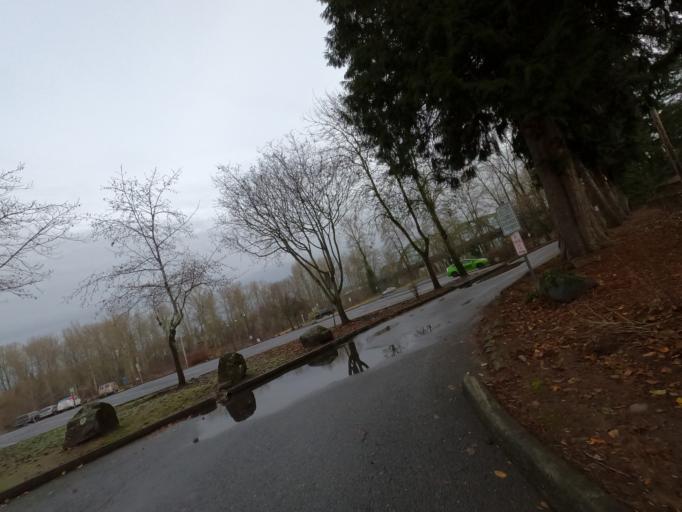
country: US
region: Oregon
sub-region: Clackamas County
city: West Linn
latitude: 45.3714
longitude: -122.6027
